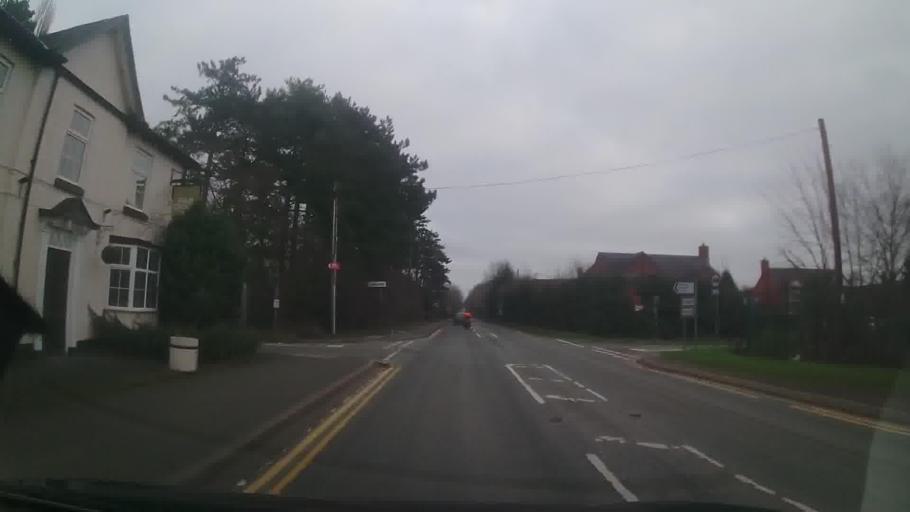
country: GB
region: England
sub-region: Shropshire
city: Bicton
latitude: 52.7235
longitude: -2.8089
